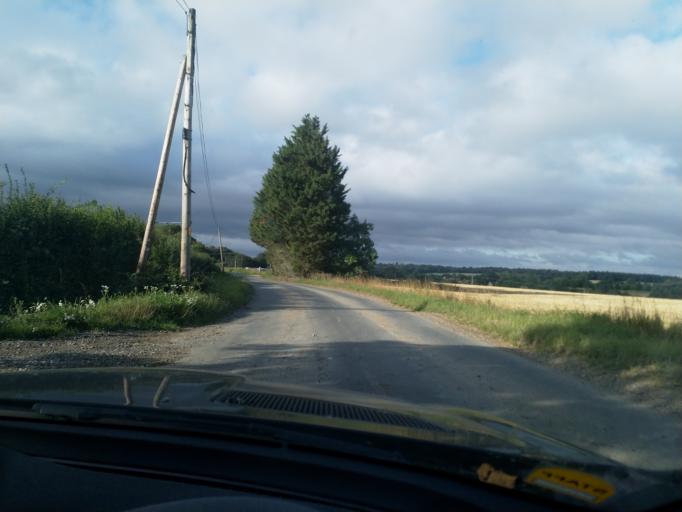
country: GB
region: England
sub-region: Suffolk
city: Elmswell
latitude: 52.2330
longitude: 0.9470
